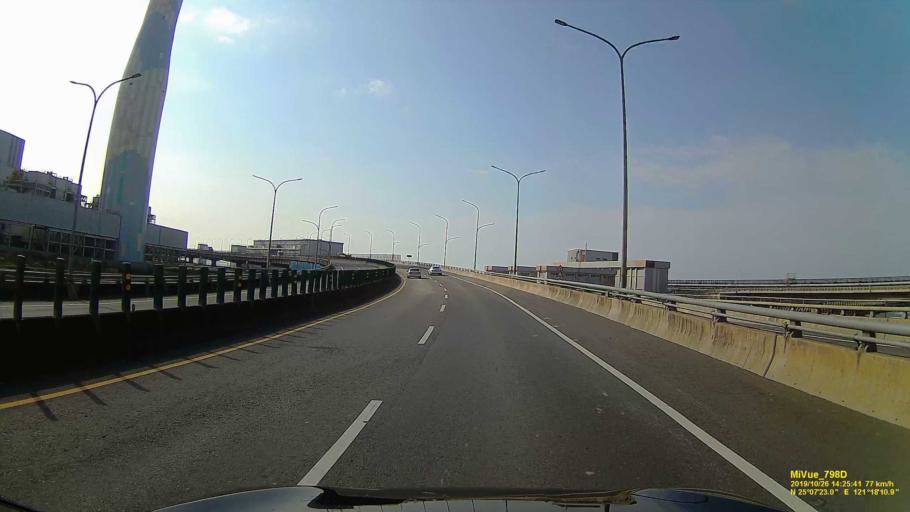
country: TW
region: Taiwan
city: Taoyuan City
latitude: 25.1229
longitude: 121.3031
